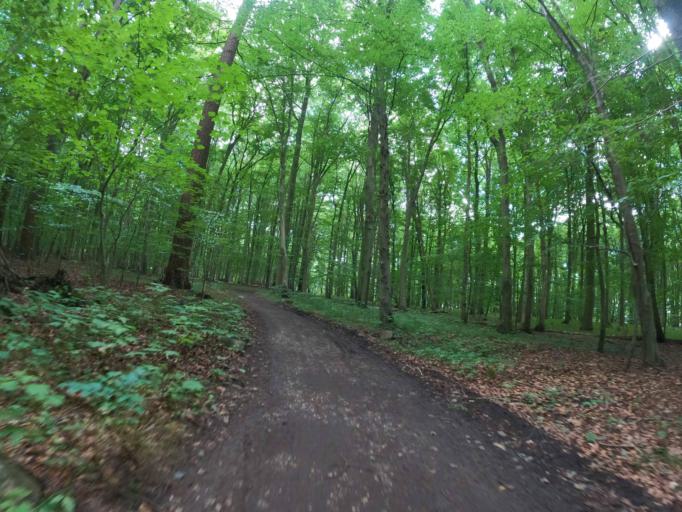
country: DE
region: Mecklenburg-Vorpommern
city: Putbus
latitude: 54.3421
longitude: 13.5301
